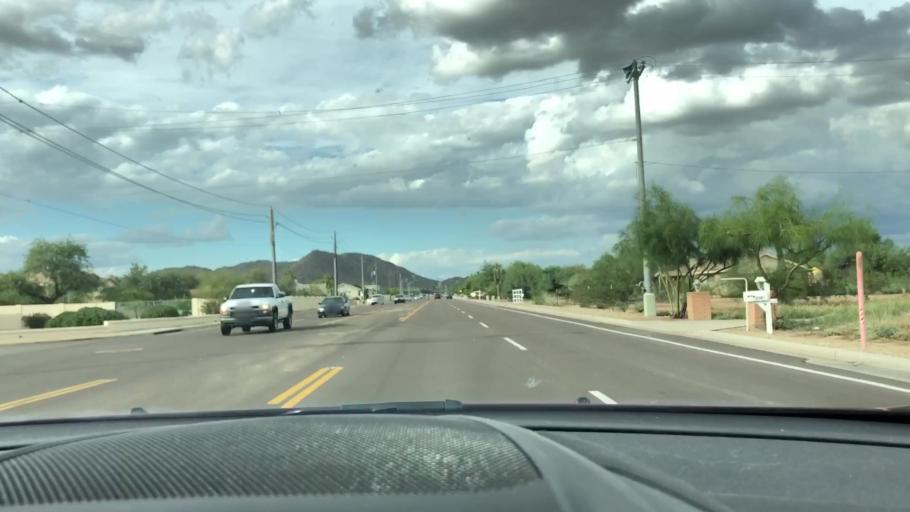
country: US
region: Arizona
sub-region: Maricopa County
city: Sun City
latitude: 33.6905
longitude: -112.2376
